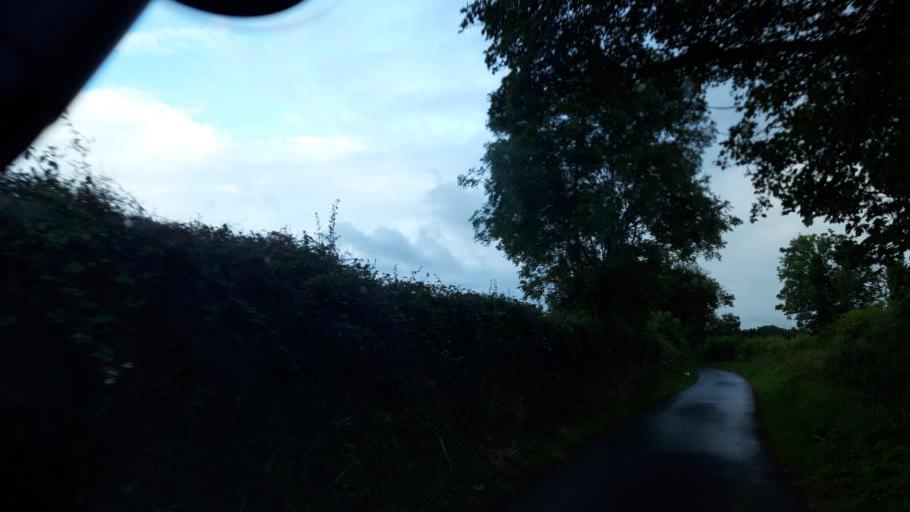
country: IE
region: Leinster
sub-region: Kildare
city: Leixlip
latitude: 53.3414
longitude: -6.4923
